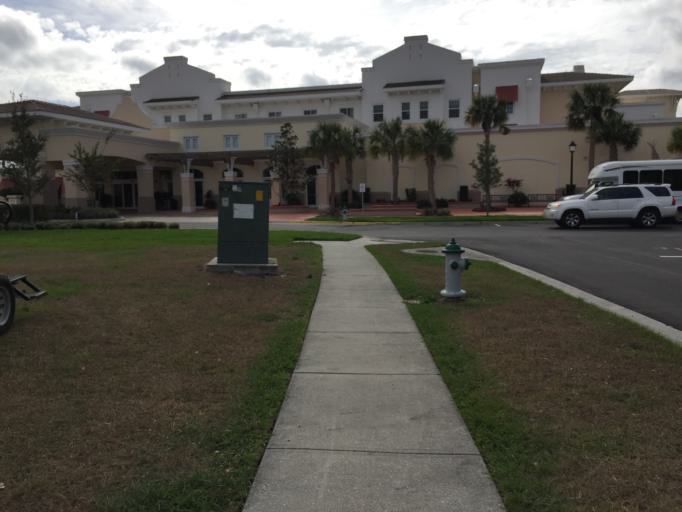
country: US
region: Florida
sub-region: Orange County
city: Bithlo
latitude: 28.5147
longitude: -81.1568
